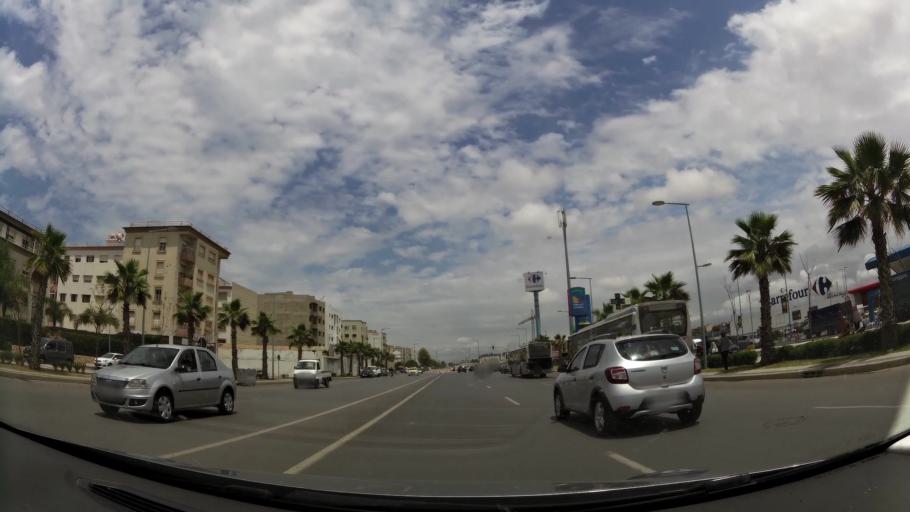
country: MA
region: Rabat-Sale-Zemmour-Zaer
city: Sale
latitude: 34.0590
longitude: -6.8038
